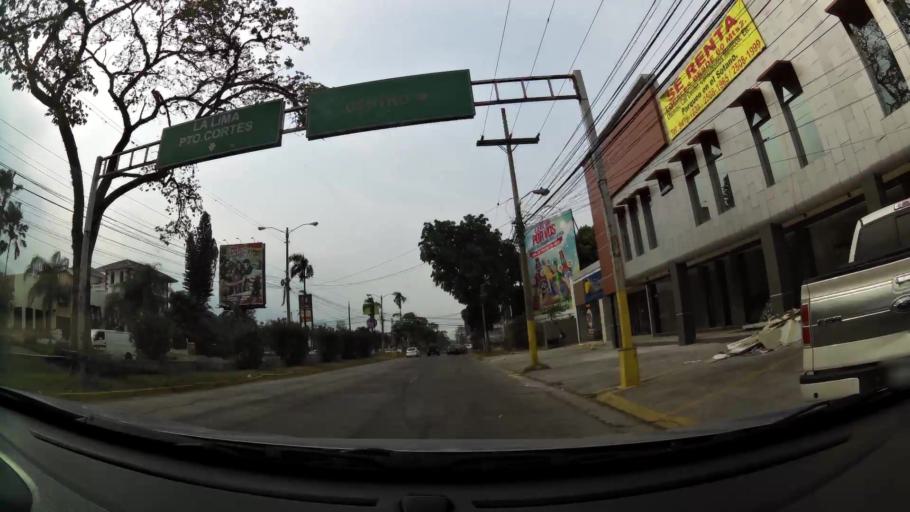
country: HN
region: Cortes
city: San Pedro Sula
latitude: 15.5060
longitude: -88.0372
